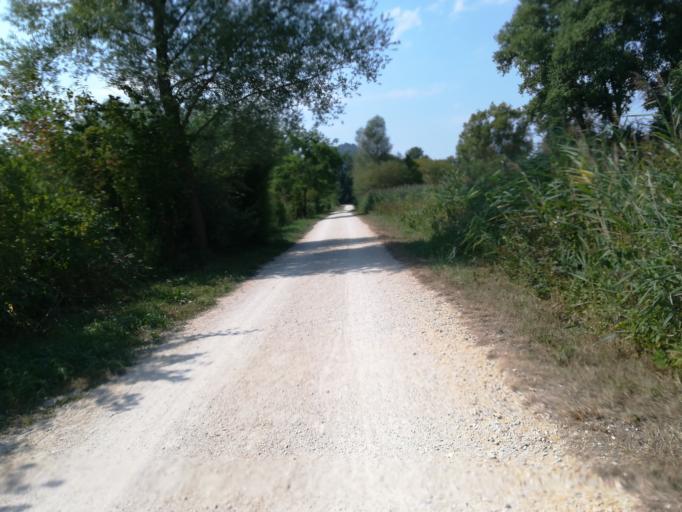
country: DE
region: Baden-Wuerttemberg
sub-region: Freiburg Region
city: Singen
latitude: 47.7845
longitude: 8.8355
